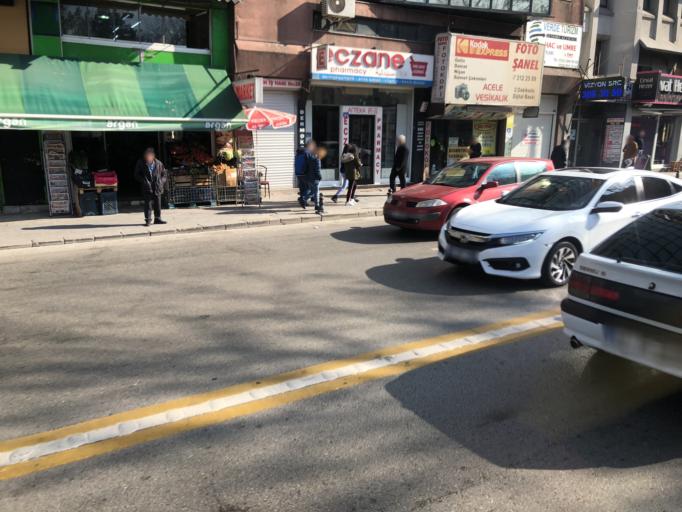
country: TR
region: Ankara
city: Ankara
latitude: 39.9458
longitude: 32.8550
